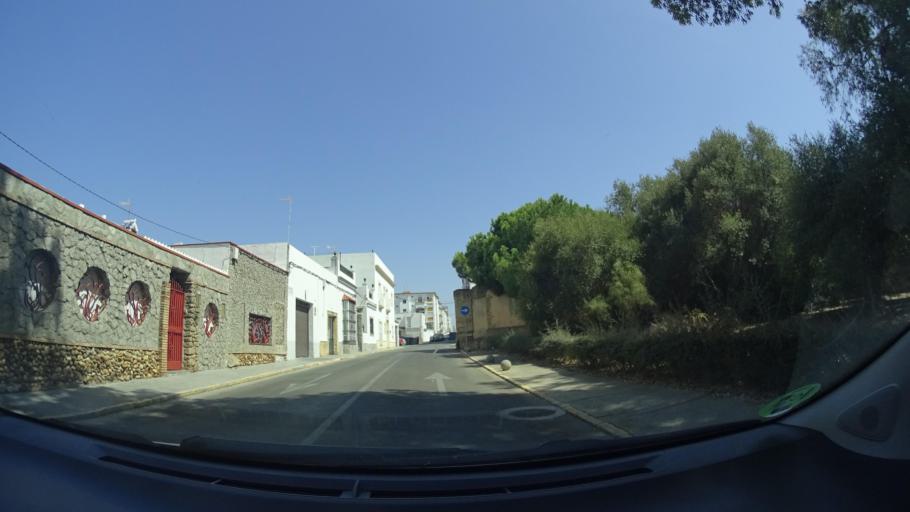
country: ES
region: Andalusia
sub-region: Provincia de Cadiz
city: San Fernando
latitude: 36.4735
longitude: -6.2007
